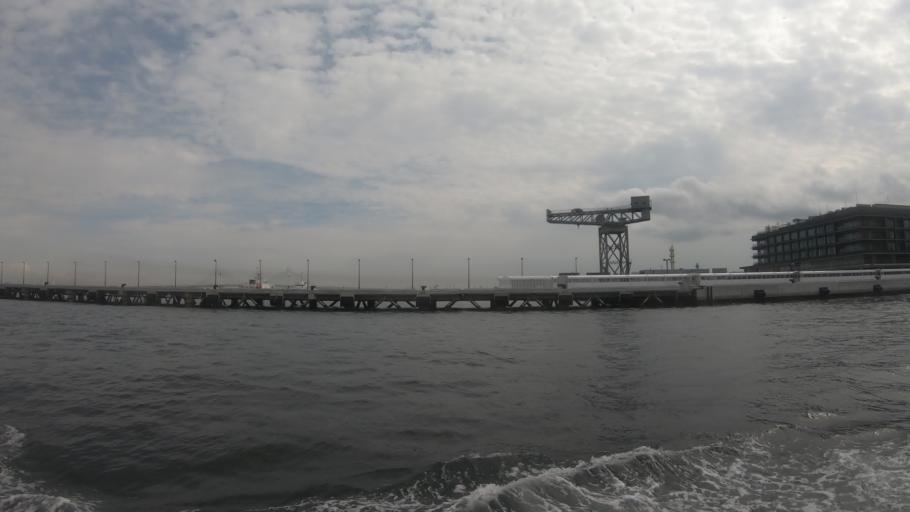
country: JP
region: Kanagawa
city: Yokohama
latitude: 35.4579
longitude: 139.6415
